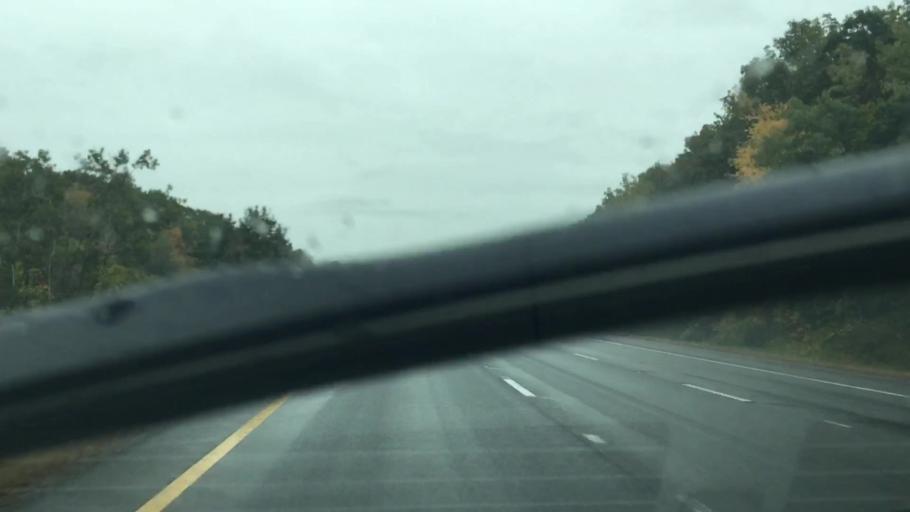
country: US
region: Massachusetts
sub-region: Essex County
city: Merrimac
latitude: 42.8168
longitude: -71.0216
